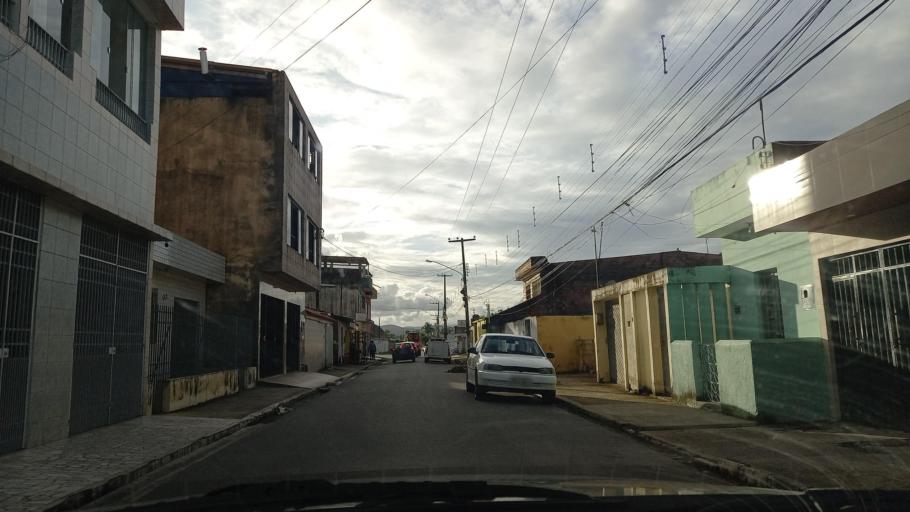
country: BR
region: Pernambuco
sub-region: Palmares
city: Palmares
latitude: -8.6825
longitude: -35.5941
